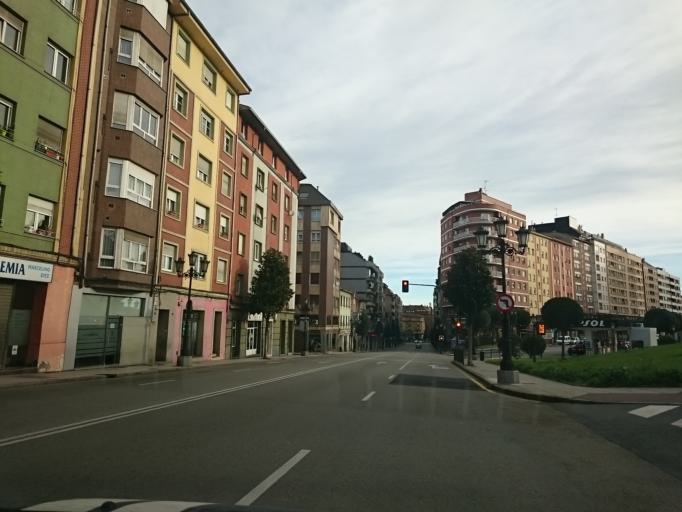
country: ES
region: Asturias
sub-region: Province of Asturias
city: Oviedo
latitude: 43.3589
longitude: -5.8666
